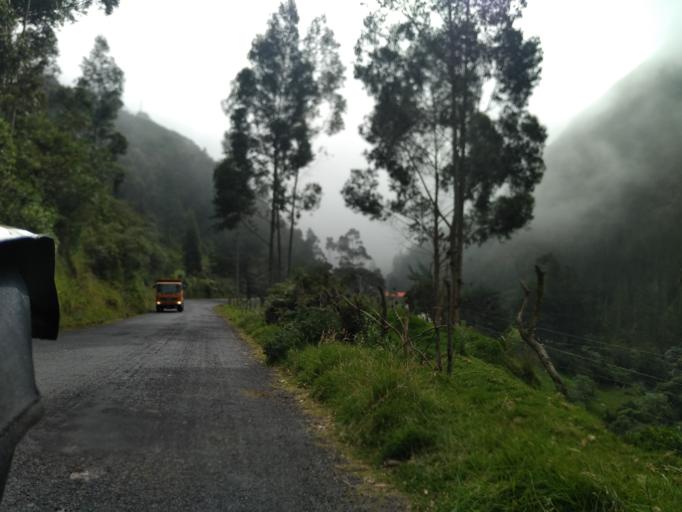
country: EC
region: Cotopaxi
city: Saquisili
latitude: -0.7001
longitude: -78.8041
